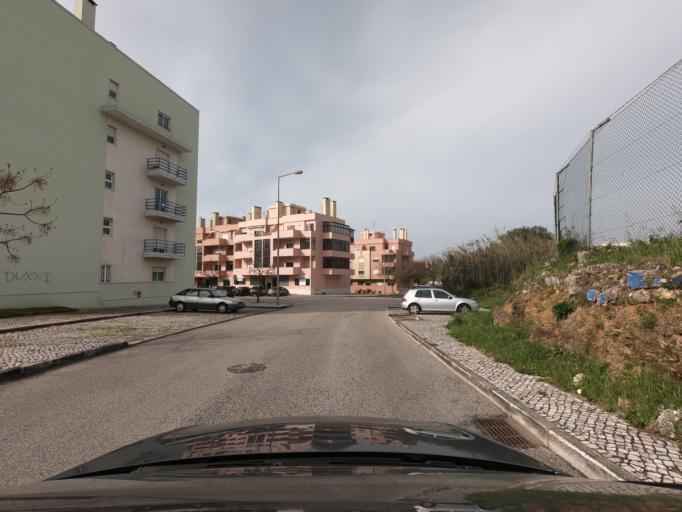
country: PT
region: Lisbon
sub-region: Cascais
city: Sao Domingos de Rana
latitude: 38.7015
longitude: -9.3224
